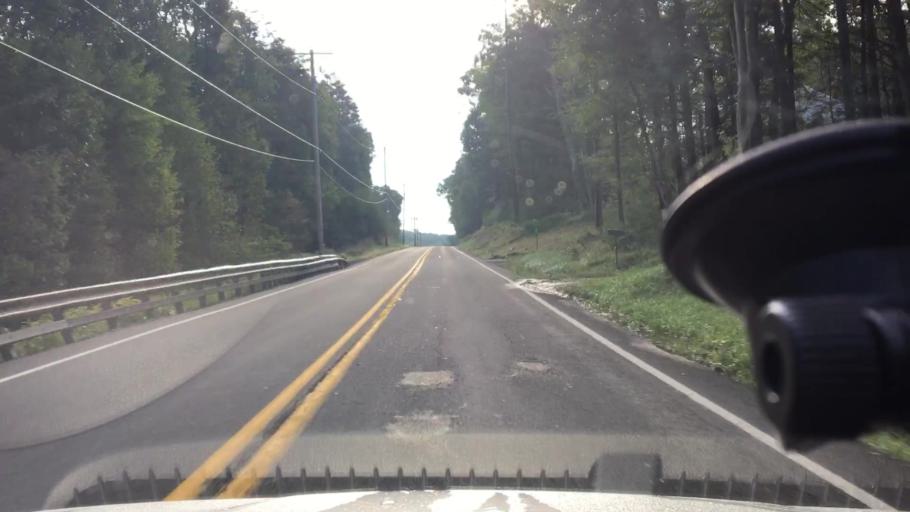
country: US
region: Pennsylvania
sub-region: Monroe County
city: Mount Pocono
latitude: 41.0999
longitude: -75.3425
